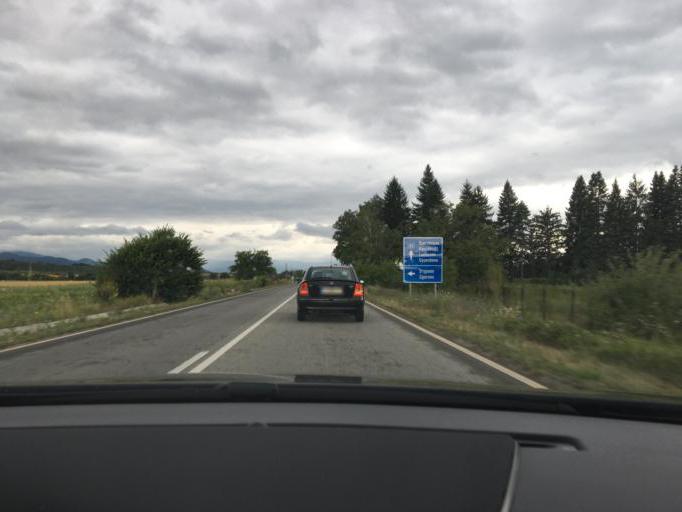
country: BG
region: Kyustendil
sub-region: Obshtina Kyustendil
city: Kyustendil
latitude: 42.2618
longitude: 22.8275
